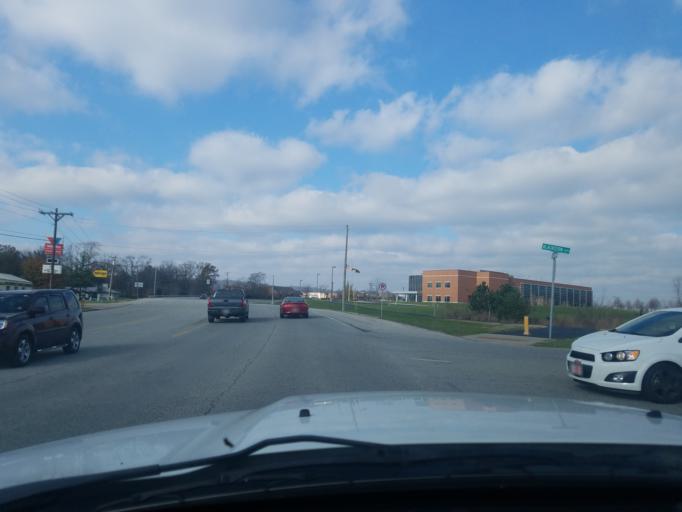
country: US
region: Indiana
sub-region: Clark County
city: Clarksville
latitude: 38.3368
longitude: -85.7986
